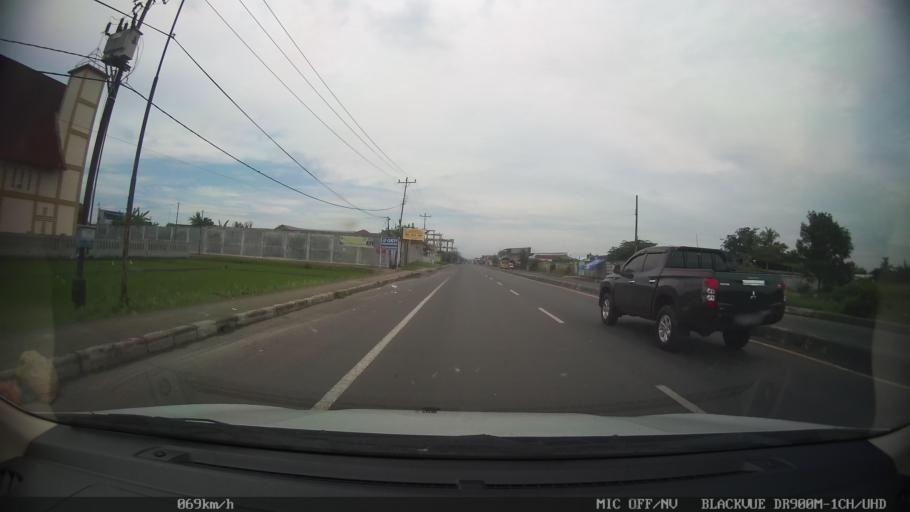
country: ID
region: North Sumatra
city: Sunggal
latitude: 3.6149
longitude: 98.5760
